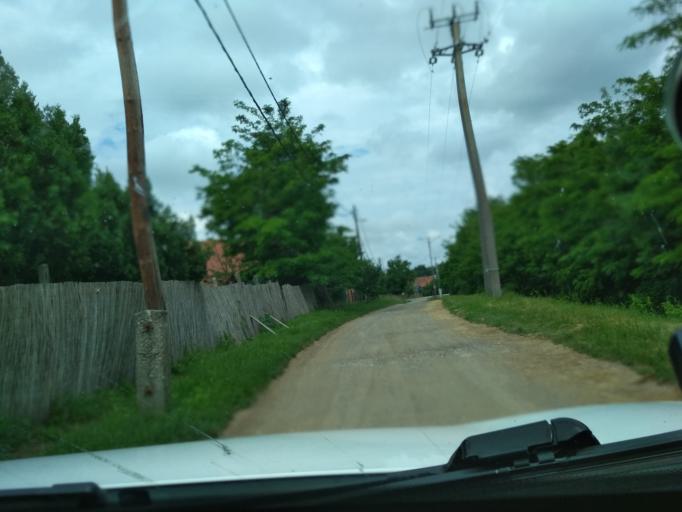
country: HU
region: Jasz-Nagykun-Szolnok
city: Tiszafured
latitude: 47.6079
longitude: 20.7289
